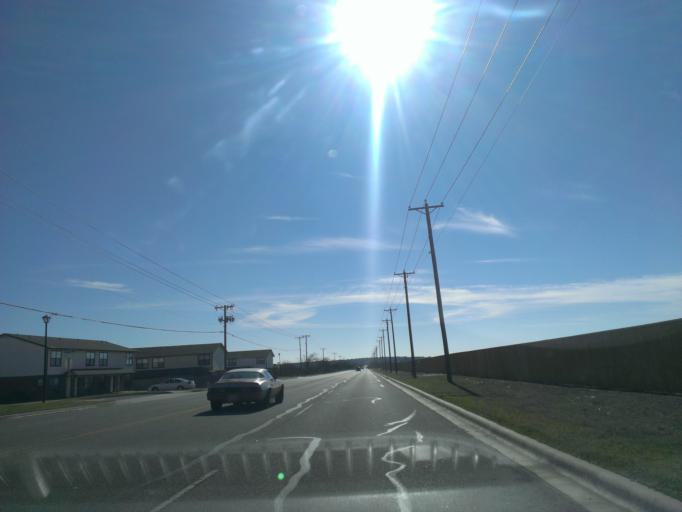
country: US
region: Texas
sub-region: Bell County
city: Harker Heights
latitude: 31.1145
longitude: -97.6659
